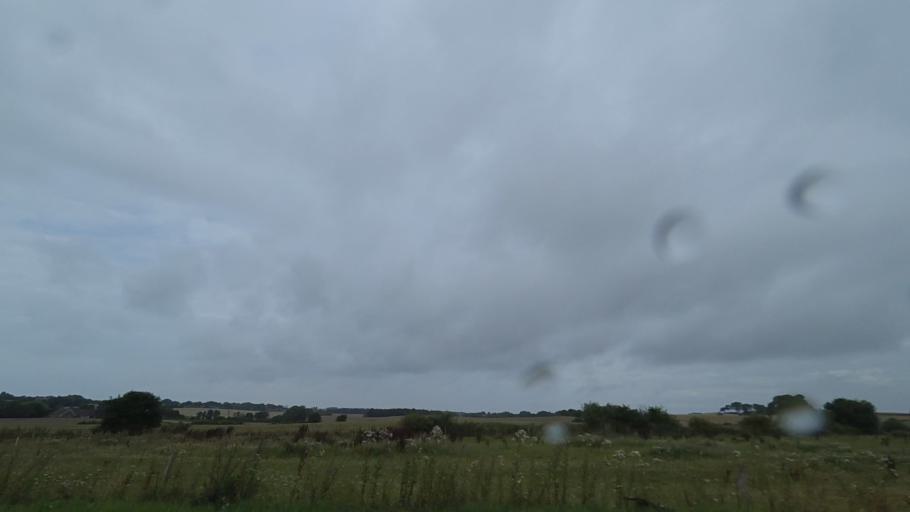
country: DK
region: Central Jutland
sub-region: Syddjurs Kommune
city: Ronde
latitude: 56.3174
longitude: 10.4599
